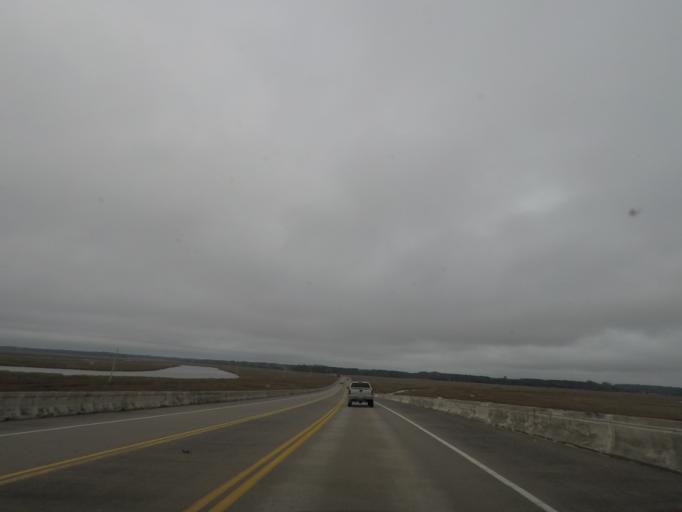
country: US
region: South Carolina
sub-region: Charleston County
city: Meggett
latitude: 32.6401
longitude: -80.3405
